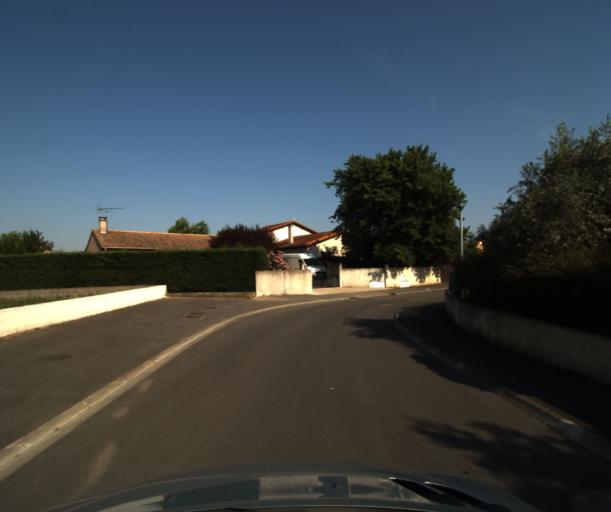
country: FR
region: Midi-Pyrenees
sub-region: Departement de la Haute-Garonne
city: Labarthe-sur-Leze
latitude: 43.4767
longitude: 1.3929
